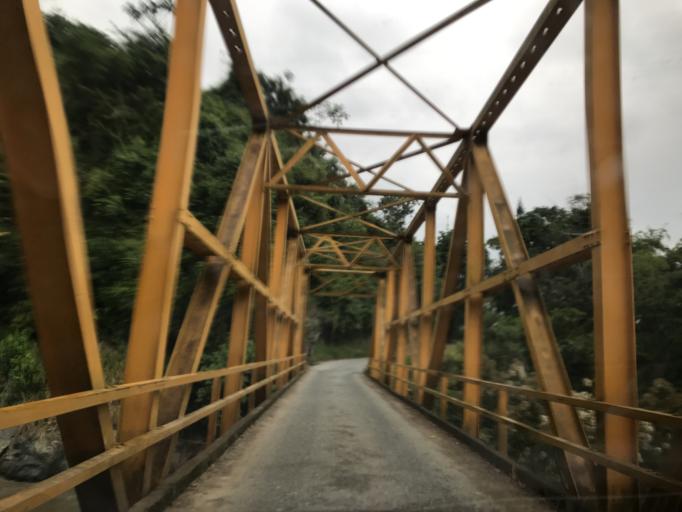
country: CO
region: Quindio
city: Genova
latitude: 4.2980
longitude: -75.7752
